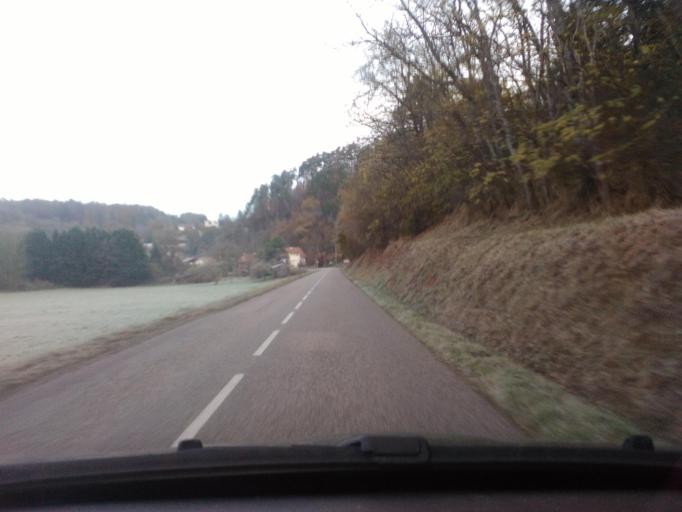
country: FR
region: Lorraine
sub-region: Departement des Vosges
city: Sainte-Marguerite
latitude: 48.2832
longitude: 6.9769
